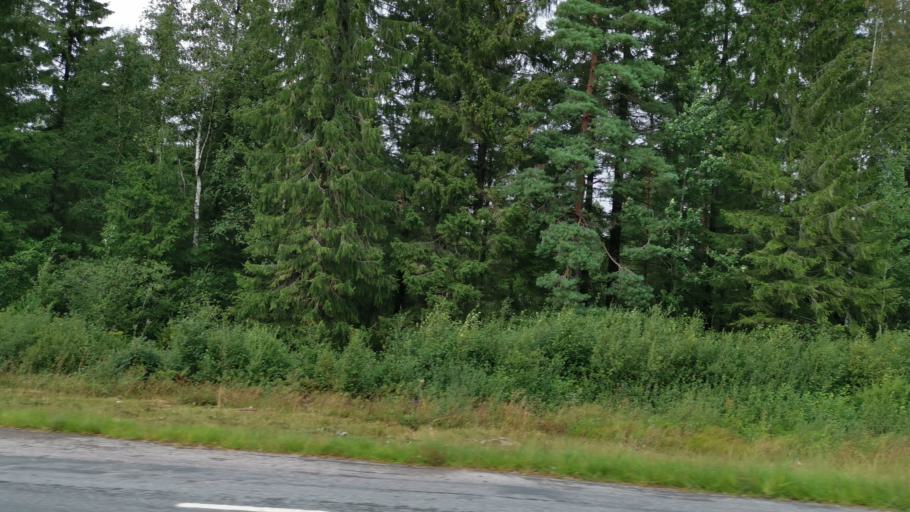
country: SE
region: Vaestra Goetaland
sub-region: Trollhattan
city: Trollhattan
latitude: 58.3270
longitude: 12.1801
